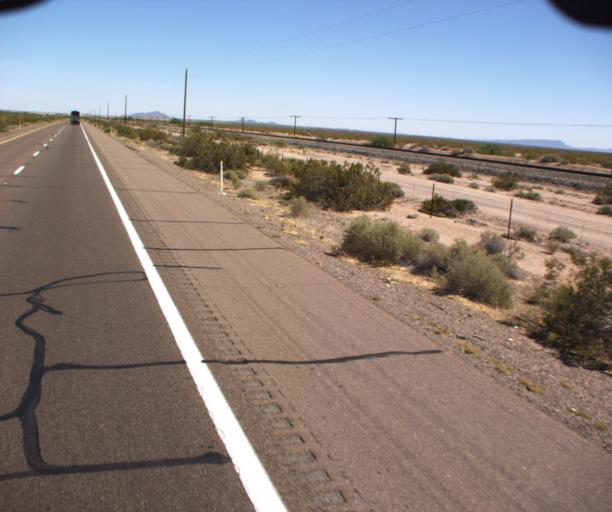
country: US
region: Arizona
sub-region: Yuma County
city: Wellton
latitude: 32.7447
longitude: -113.6766
